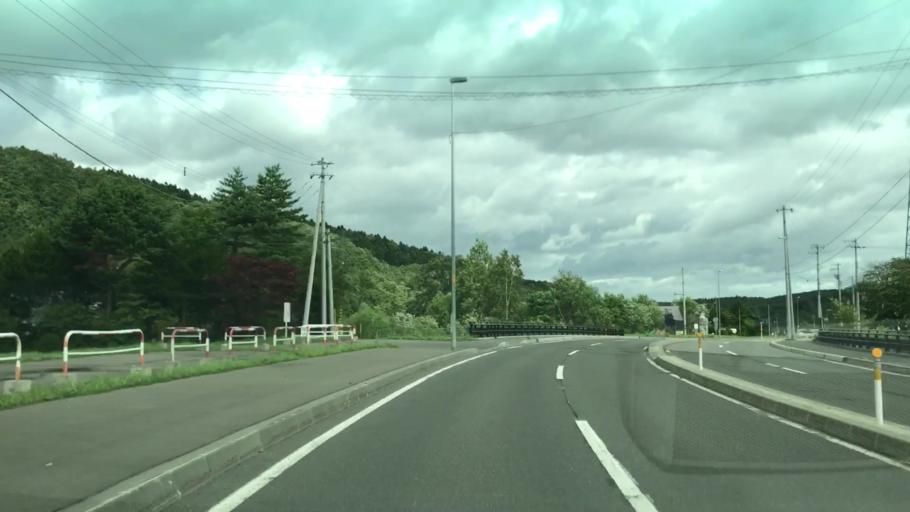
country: JP
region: Hokkaido
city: Kitahiroshima
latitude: 42.9525
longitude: 141.4513
